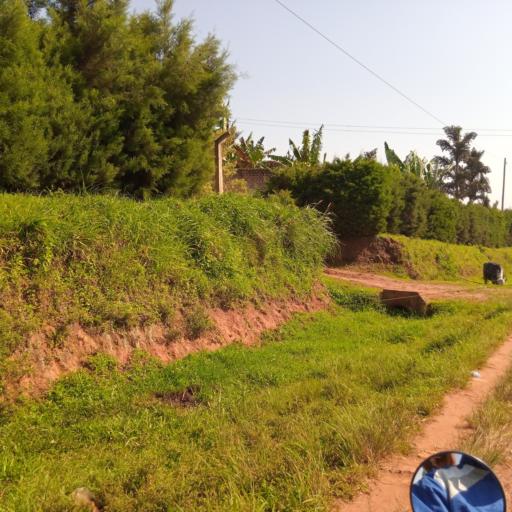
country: UG
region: Central Region
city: Masaka
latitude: -0.3585
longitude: 31.7207
